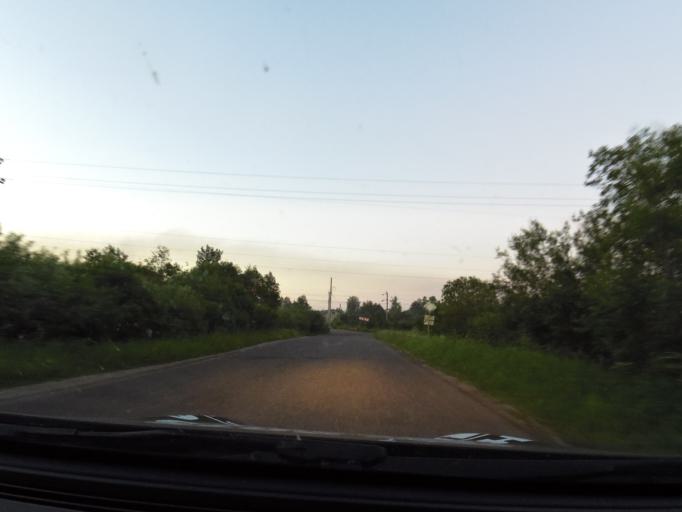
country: RU
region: Kostroma
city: Buy
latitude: 58.4856
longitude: 41.5038
